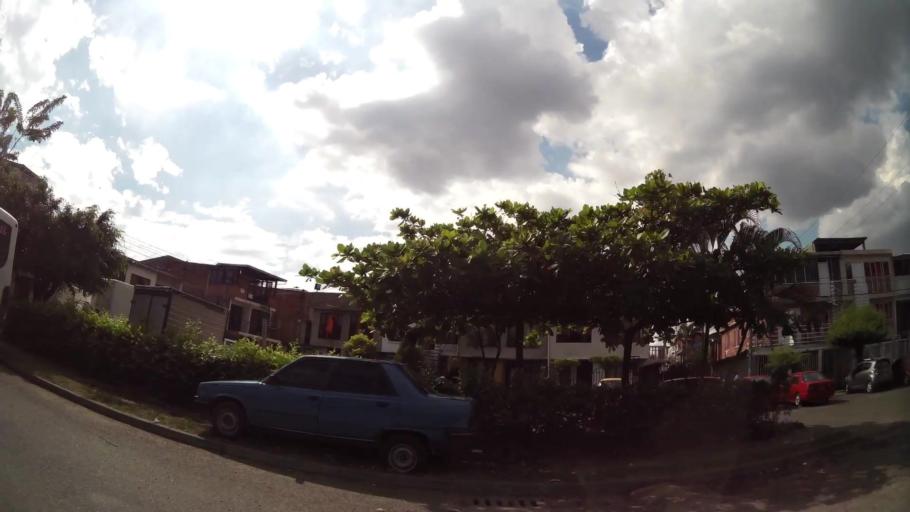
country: CO
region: Valle del Cauca
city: Cali
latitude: 3.3948
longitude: -76.5034
